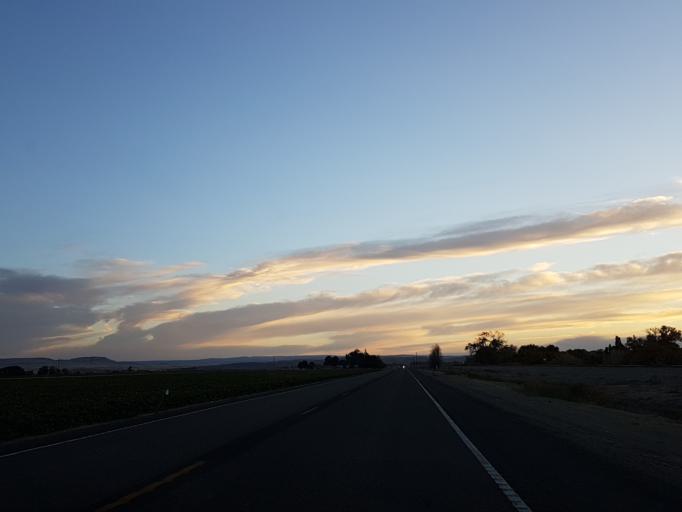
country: US
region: Oregon
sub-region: Malheur County
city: Vale
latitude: 43.9634
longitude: -117.2772
